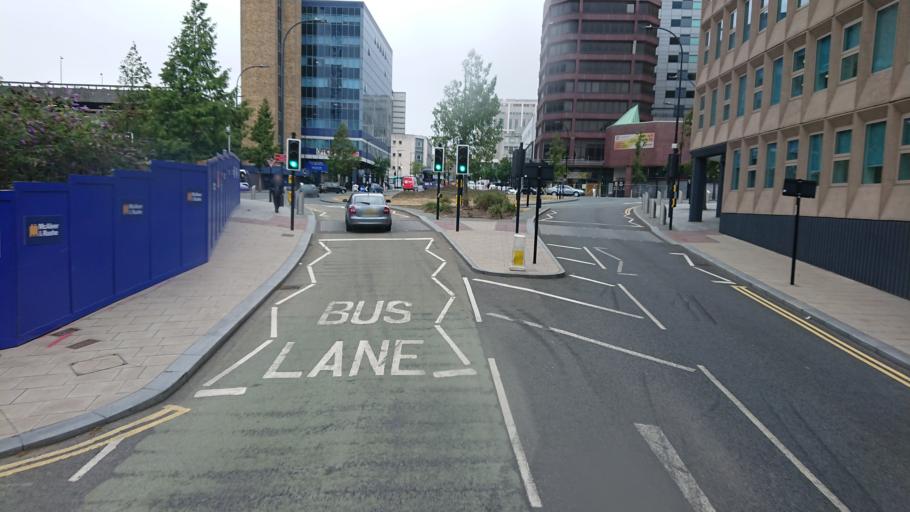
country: GB
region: England
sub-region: Sheffield
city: Sheffield
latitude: 53.3770
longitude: -1.4692
